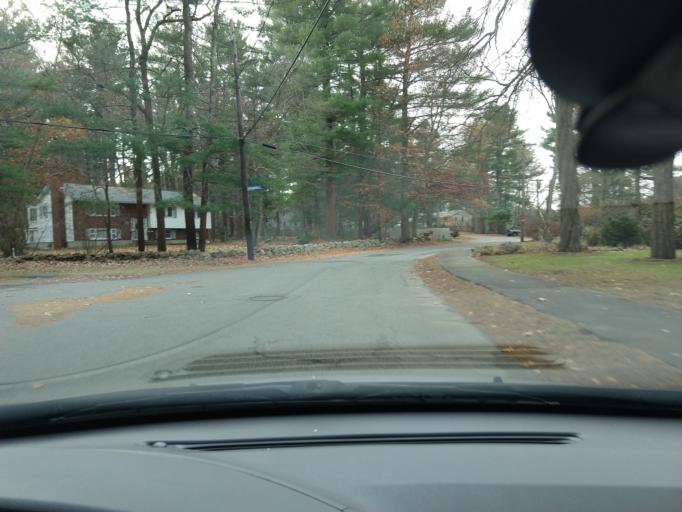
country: US
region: Massachusetts
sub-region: Middlesex County
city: Bedford
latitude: 42.5052
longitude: -71.2512
